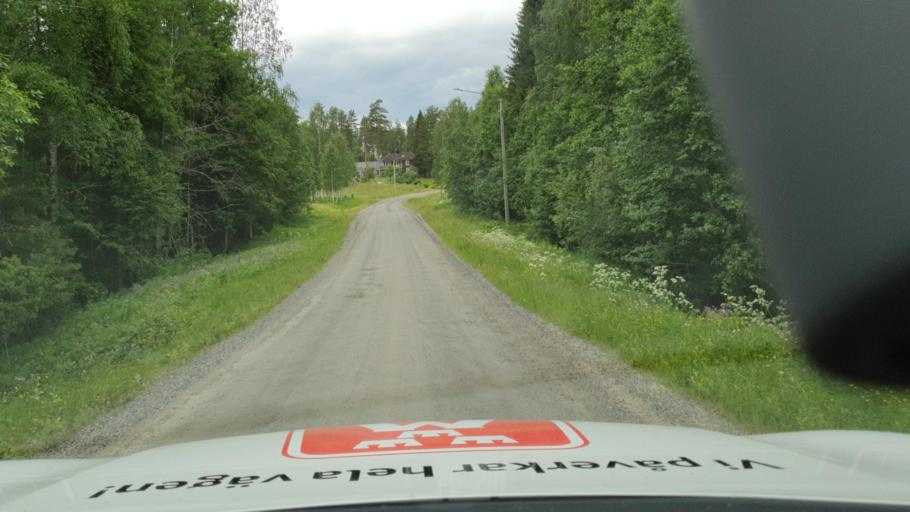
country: SE
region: Vaesterbotten
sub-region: Bjurholms Kommun
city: Bjurholm
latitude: 63.7420
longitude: 19.2809
